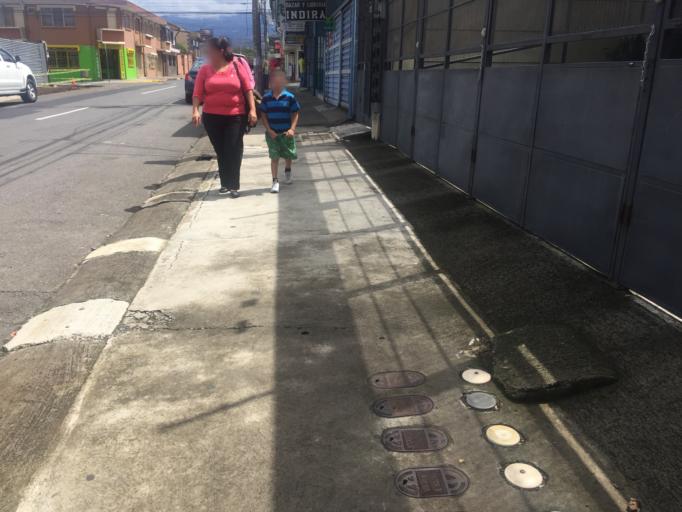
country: CR
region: Heredia
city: Heredia
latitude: 10.0012
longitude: -84.1192
